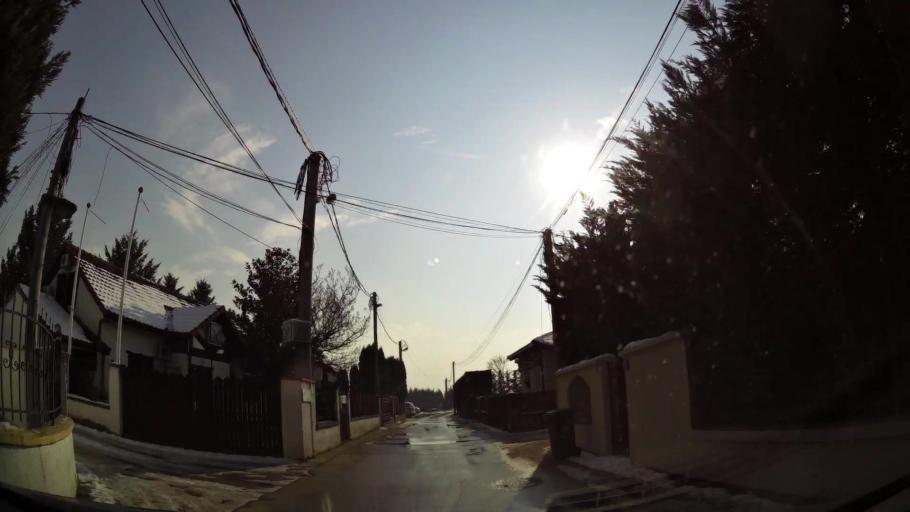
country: MK
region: Suto Orizari
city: Suto Orizare
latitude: 42.0261
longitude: 21.3880
